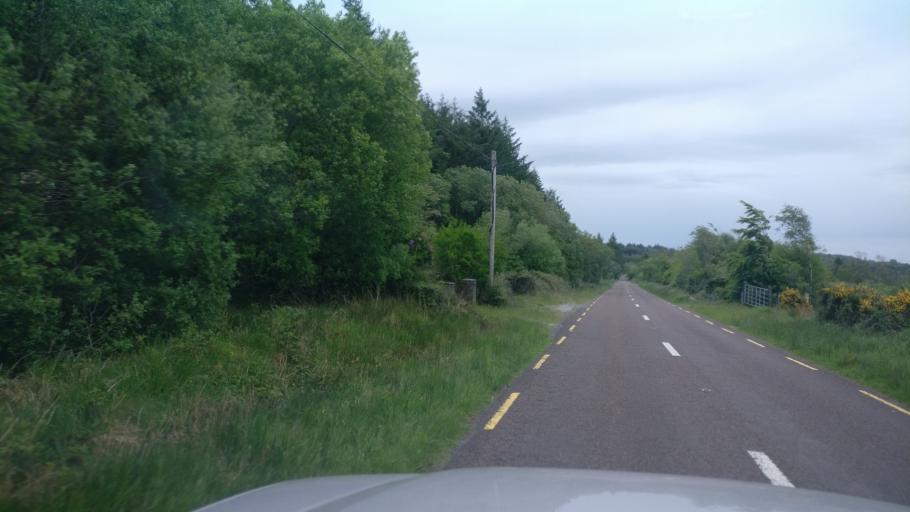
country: IE
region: Connaught
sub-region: County Galway
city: Loughrea
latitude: 53.0823
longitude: -8.5237
